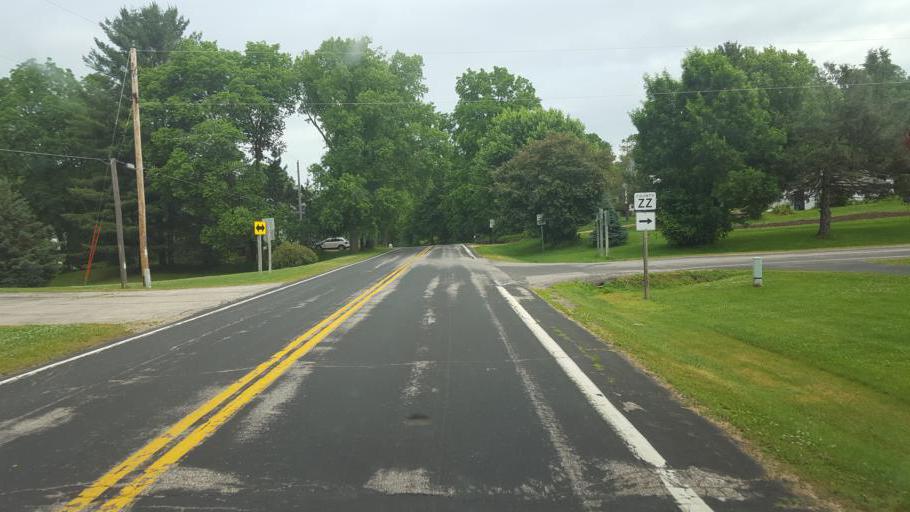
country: US
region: Wisconsin
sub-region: Monroe County
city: Cashton
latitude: 43.7195
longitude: -90.5859
